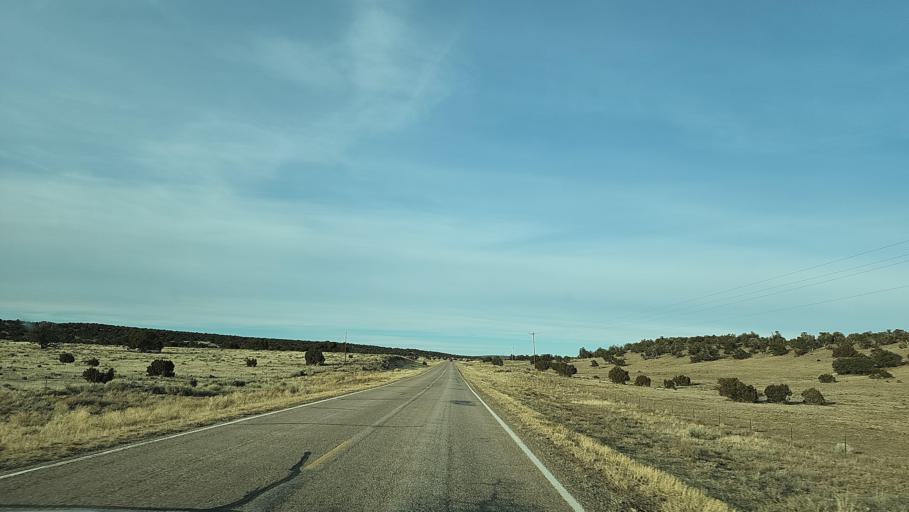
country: US
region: New Mexico
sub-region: Catron County
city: Reserve
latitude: 34.3935
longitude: -108.4466
